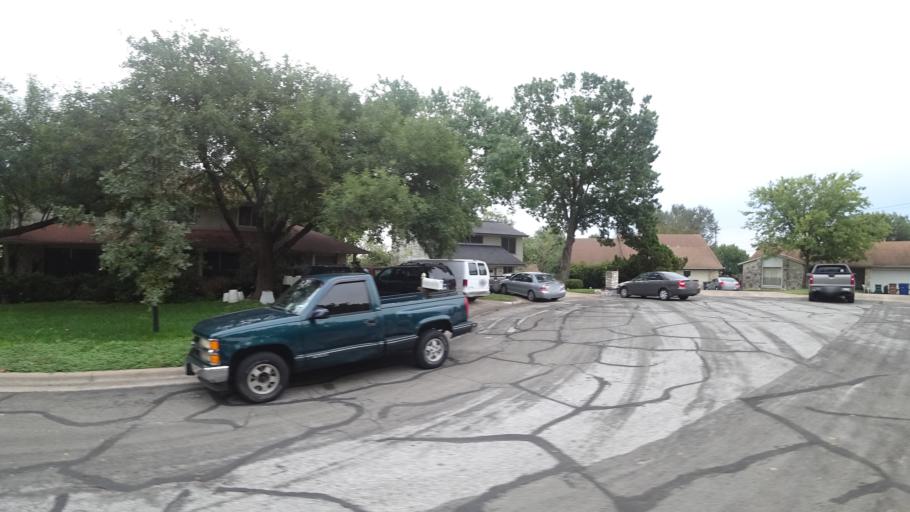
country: US
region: Texas
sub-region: Travis County
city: Austin
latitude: 30.3417
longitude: -97.6908
